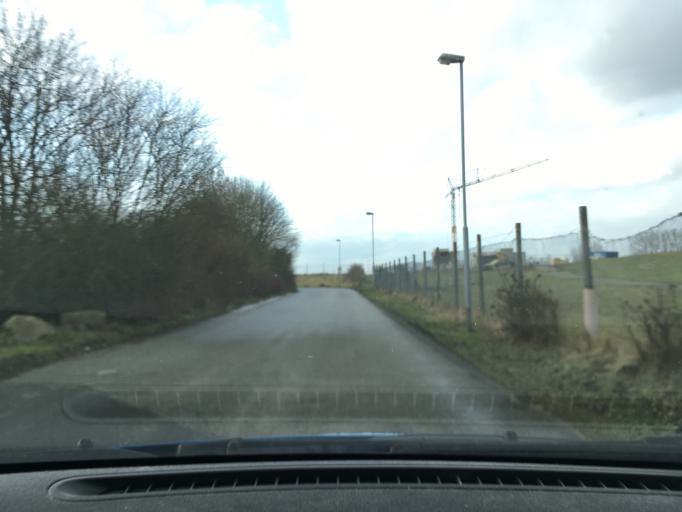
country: DE
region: Schleswig-Holstein
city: Wedel
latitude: 53.5765
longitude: 9.6781
